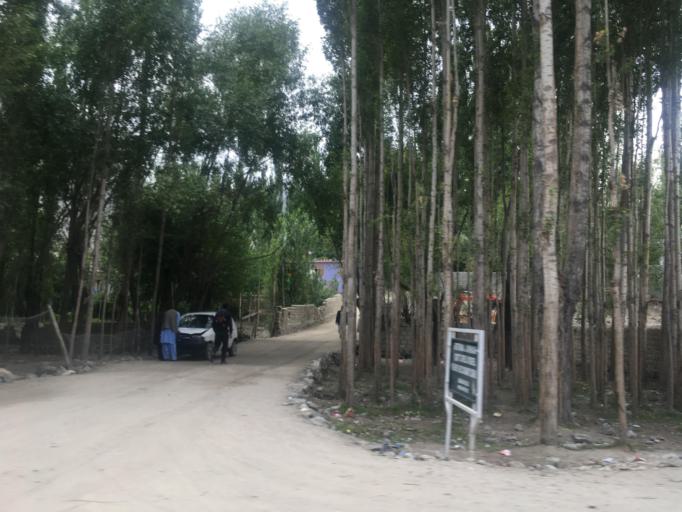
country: PK
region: Gilgit-Baltistan
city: Skardu
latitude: 35.2927
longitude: 75.6128
